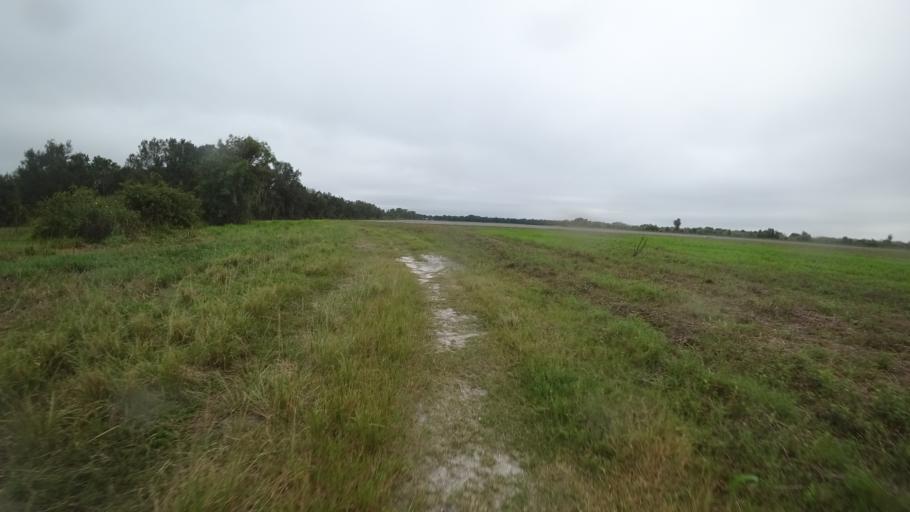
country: US
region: Florida
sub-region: Sarasota County
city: Warm Mineral Springs
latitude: 27.2815
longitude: -82.1349
